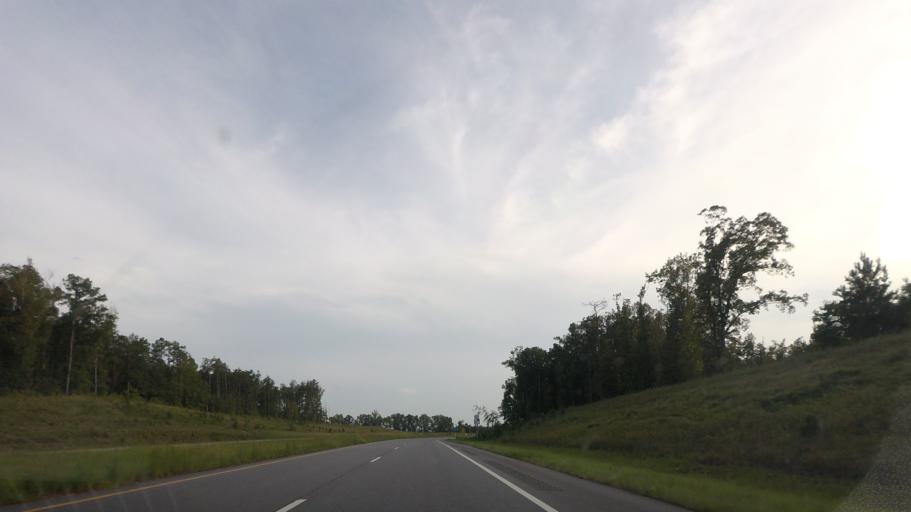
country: US
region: Georgia
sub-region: Wilkinson County
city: Gordon
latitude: 32.8622
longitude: -83.3783
